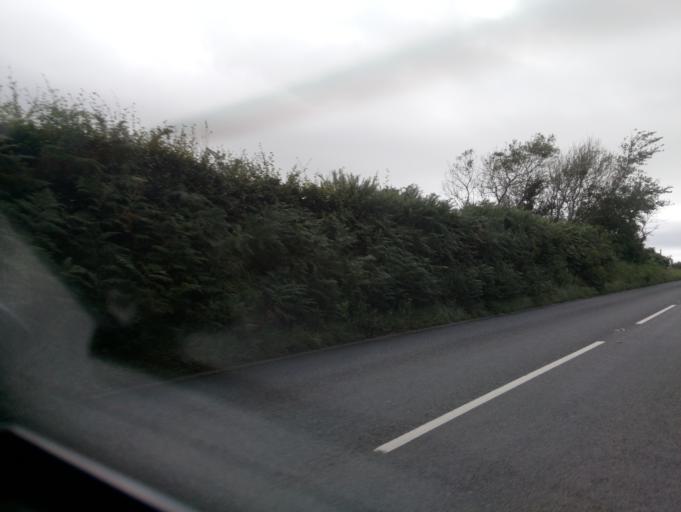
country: GB
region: England
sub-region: Devon
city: Kingsbridge
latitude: 50.2961
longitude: -3.7945
